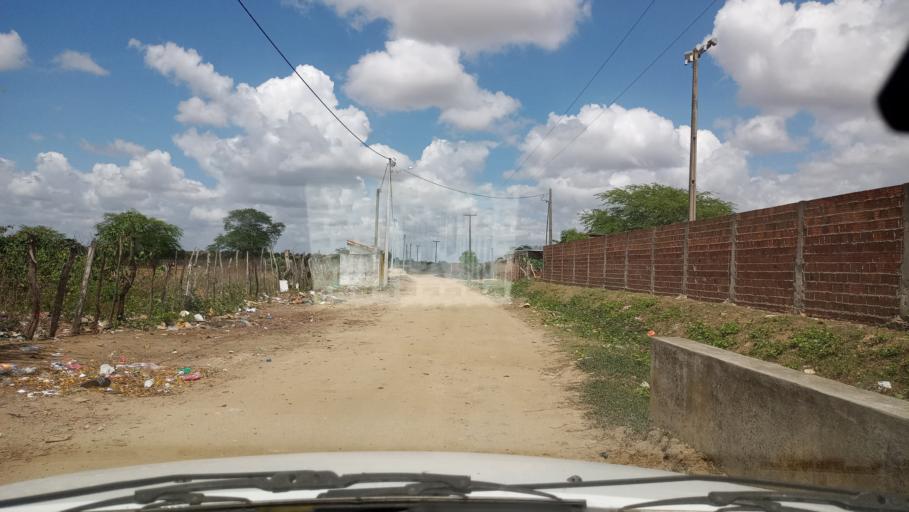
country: BR
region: Rio Grande do Norte
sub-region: Santo Antonio
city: Santo Antonio
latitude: -6.3477
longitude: -35.3767
